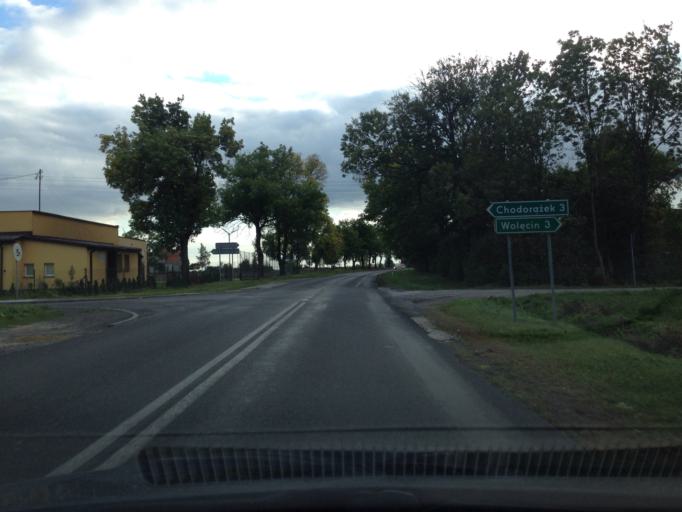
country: PL
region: Kujawsko-Pomorskie
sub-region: Powiat lipnowski
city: Lipno
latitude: 52.8909
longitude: 19.2088
